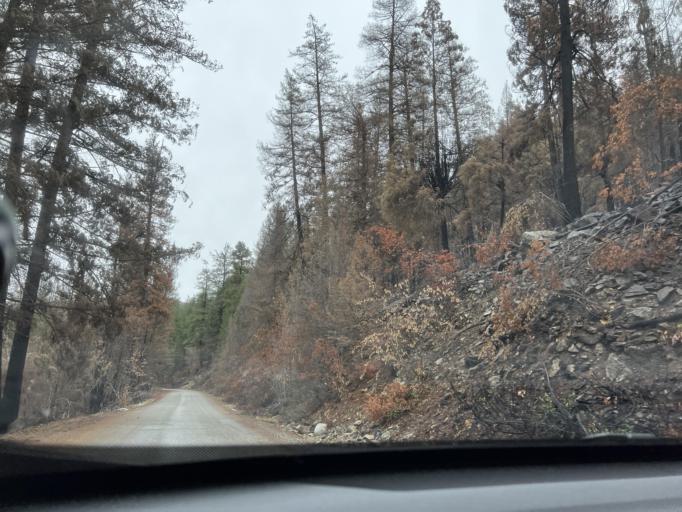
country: US
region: Washington
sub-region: Okanogan County
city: Brewster
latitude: 48.5682
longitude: -120.1730
